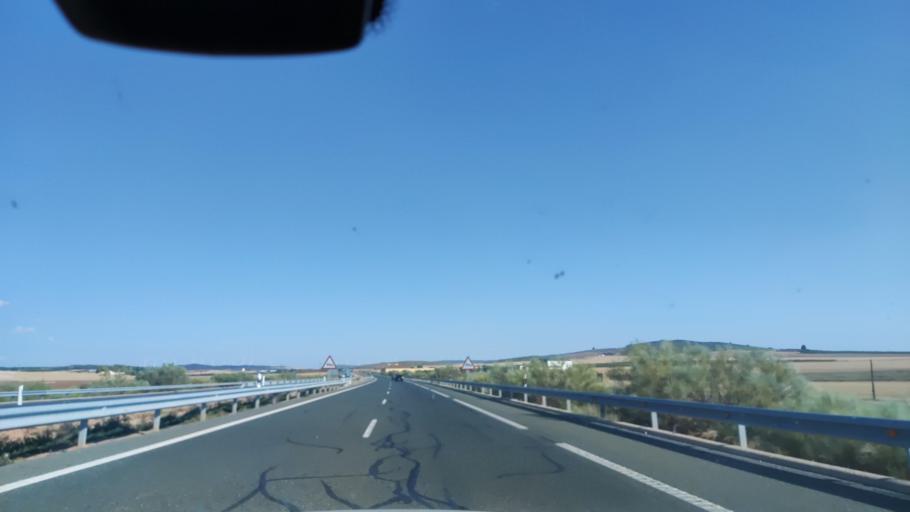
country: ES
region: Castille-La Mancha
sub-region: Provincia de Albacete
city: Pozo-Canada
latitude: 38.8439
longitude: -1.7628
